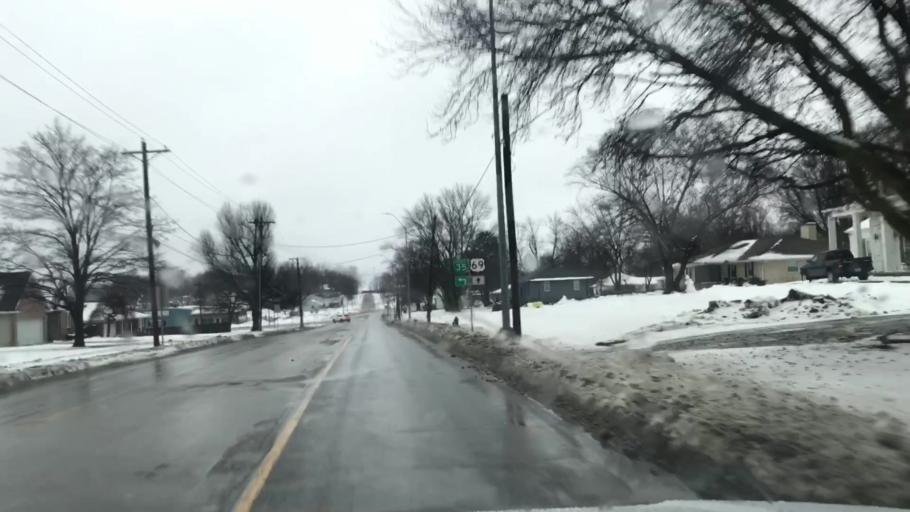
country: US
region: Missouri
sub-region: Clinton County
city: Cameron
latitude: 39.7335
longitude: -94.2361
